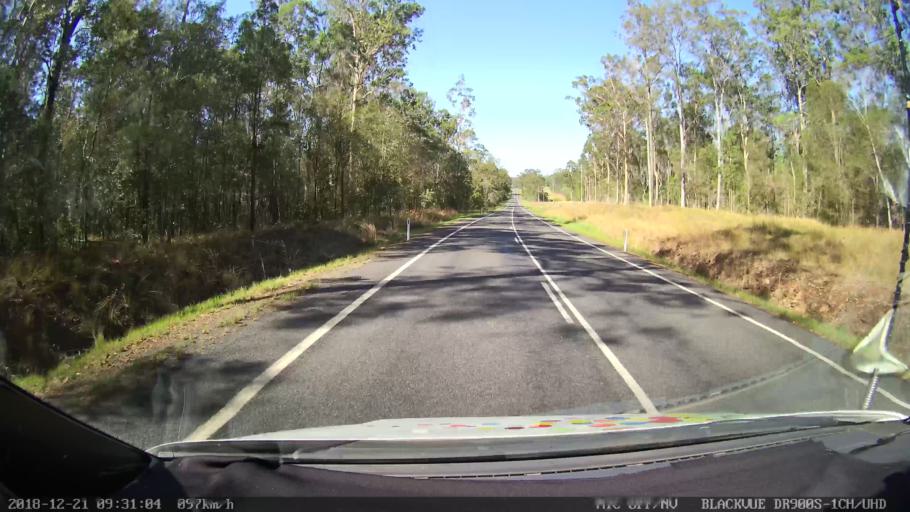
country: AU
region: New South Wales
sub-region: Clarence Valley
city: Maclean
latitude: -29.4558
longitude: 152.9929
